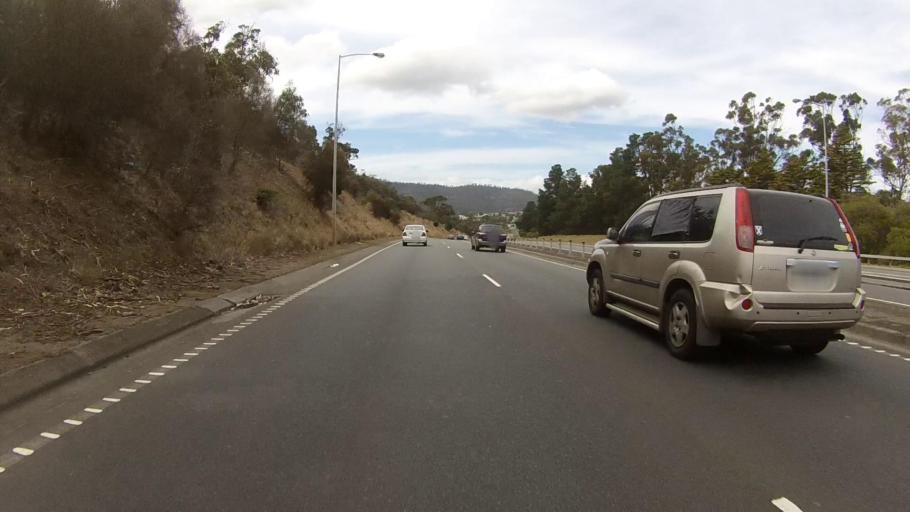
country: AU
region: Tasmania
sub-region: Clarence
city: Lindisfarne
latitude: -42.8616
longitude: 147.3657
